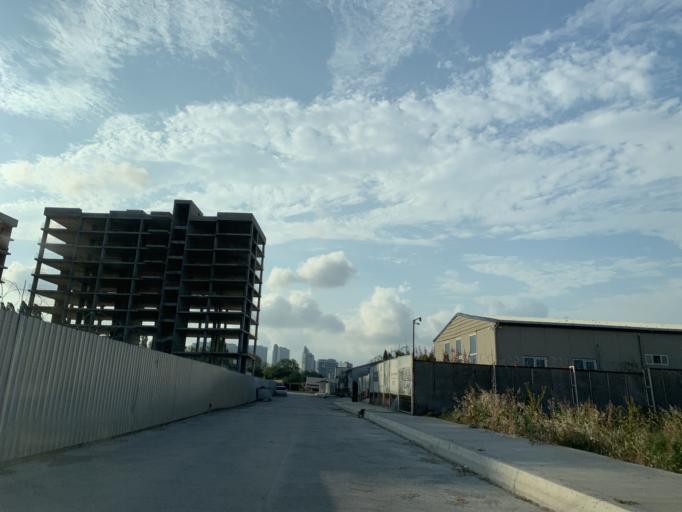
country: TR
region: Istanbul
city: Esenyurt
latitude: 41.0464
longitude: 28.6776
